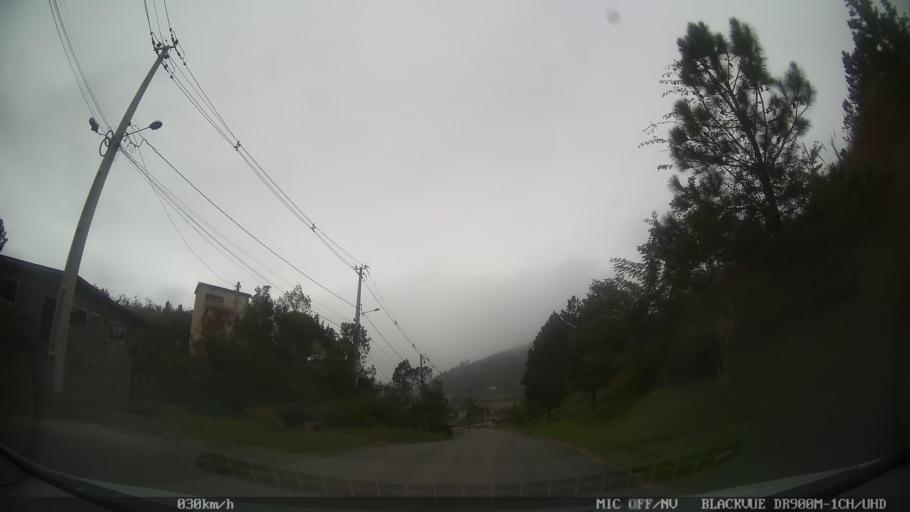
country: BR
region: Parana
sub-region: Campina Grande Do Sul
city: Campina Grande do Sul
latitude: -25.1083
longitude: -48.8325
